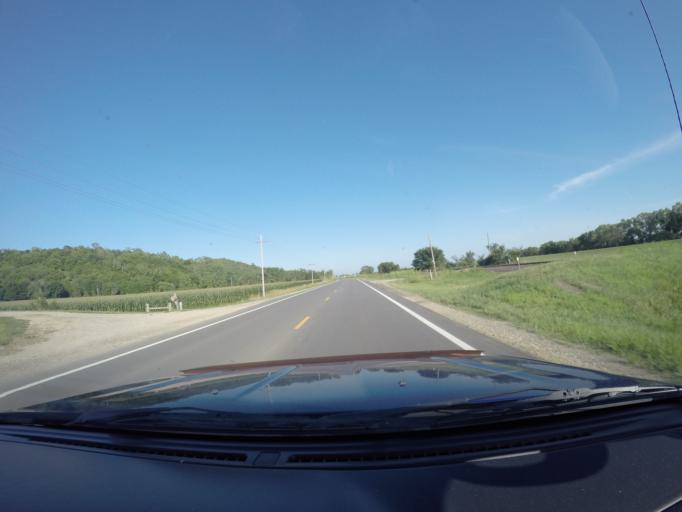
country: US
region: Kansas
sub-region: Douglas County
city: Lawrence
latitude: 39.0477
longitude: -95.2763
